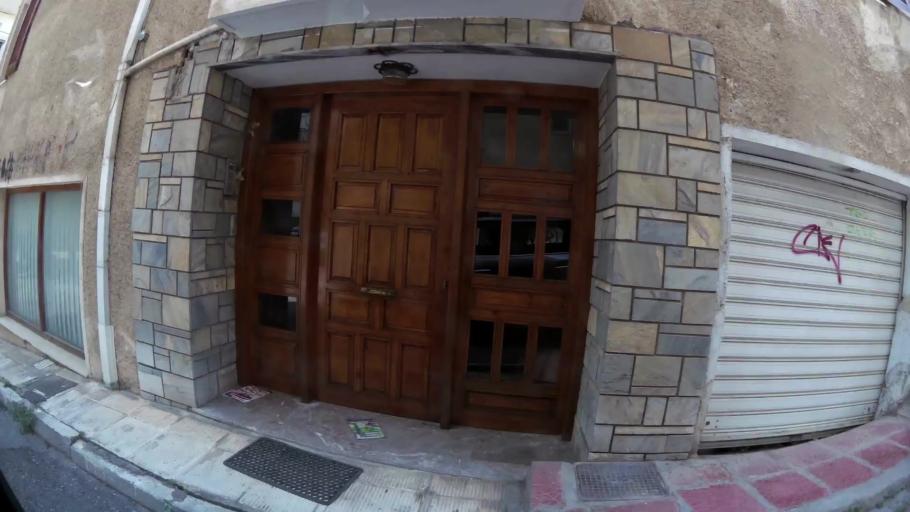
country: GR
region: West Macedonia
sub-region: Nomos Kozanis
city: Kozani
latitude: 40.3040
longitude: 21.7865
